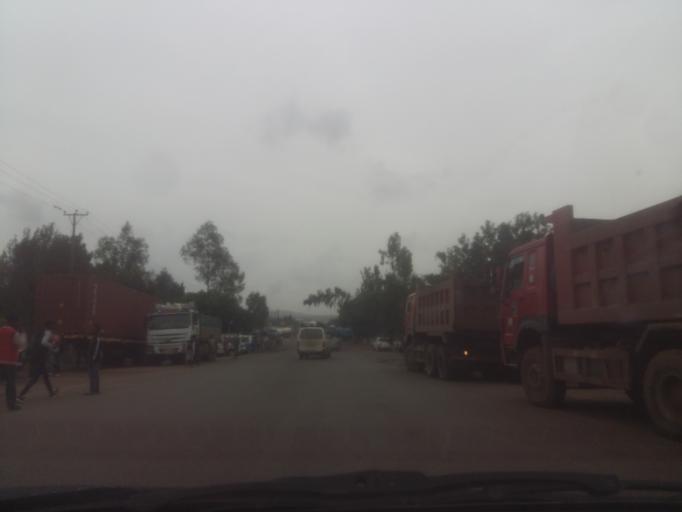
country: ET
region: Oromiya
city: Bishoftu
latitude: 8.7950
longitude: 38.8994
